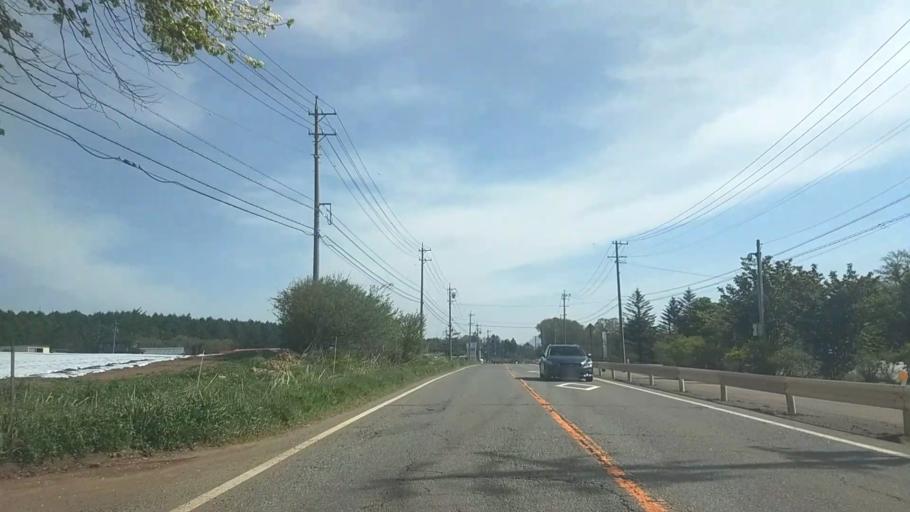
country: JP
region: Nagano
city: Saku
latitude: 35.9683
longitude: 138.4776
